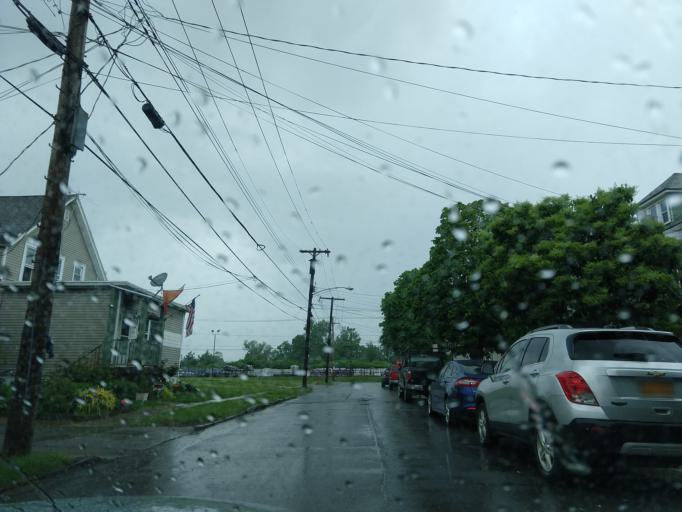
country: US
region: New York
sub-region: Erie County
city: Kenmore
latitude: 42.9426
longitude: -78.8833
